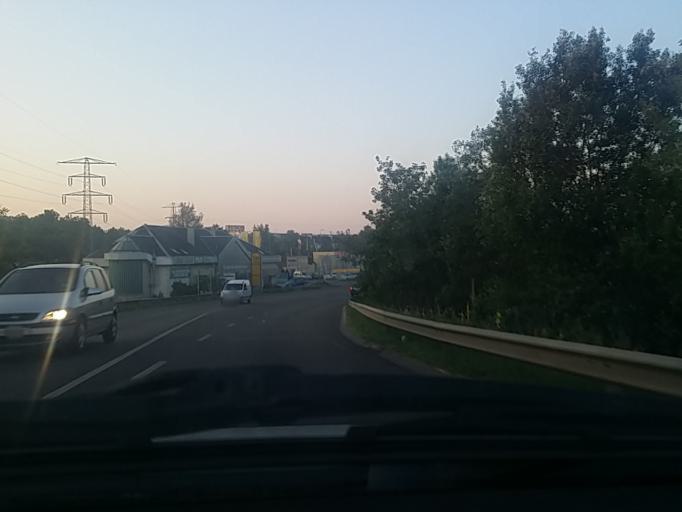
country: HU
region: Budapest
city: Budapest XVII. keruelet
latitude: 47.4861
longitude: 19.2282
